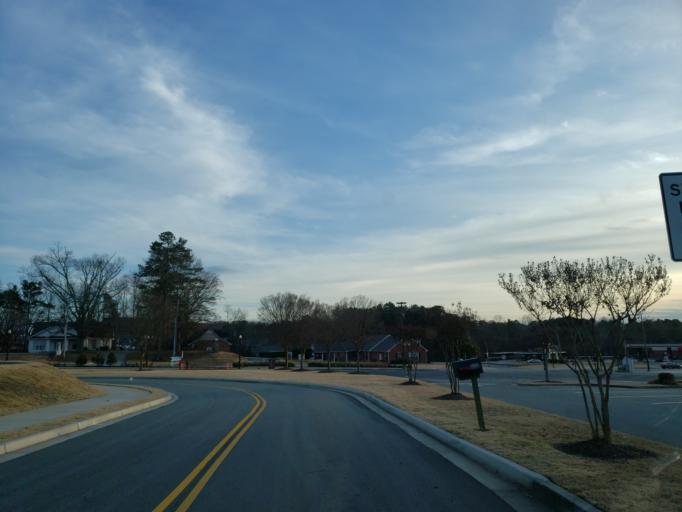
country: US
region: Georgia
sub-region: Cobb County
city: Kennesaw
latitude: 34.0216
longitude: -84.6204
